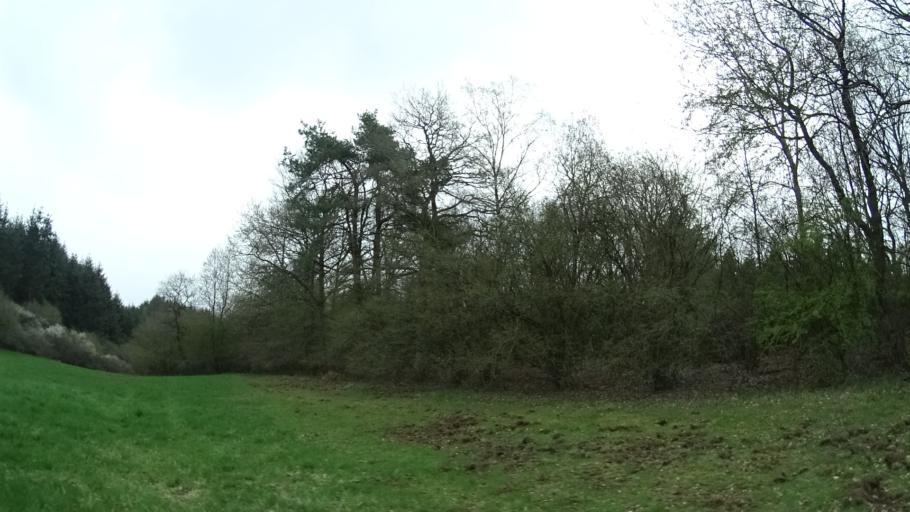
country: DE
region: Rheinland-Pfalz
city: Gerach
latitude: 49.7514
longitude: 7.3211
